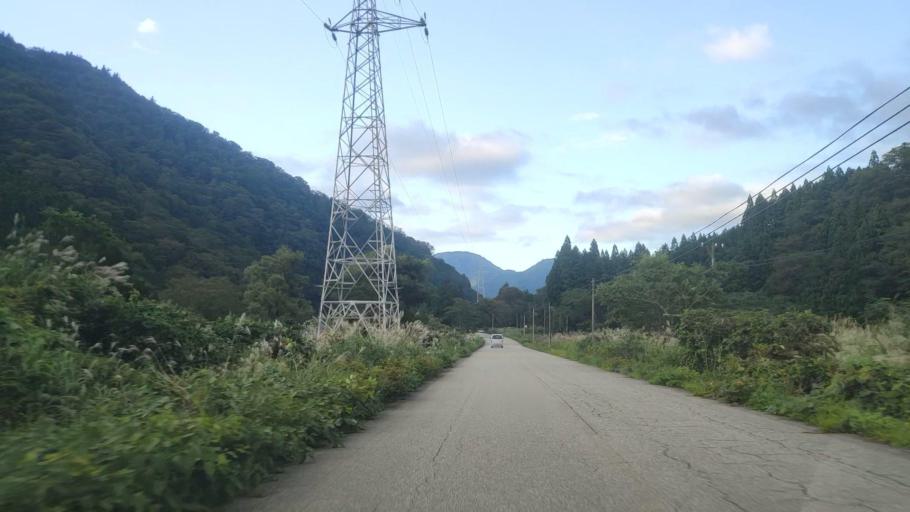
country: JP
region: Toyama
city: Yatsuomachi-higashikumisaka
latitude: 36.4579
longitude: 137.0846
